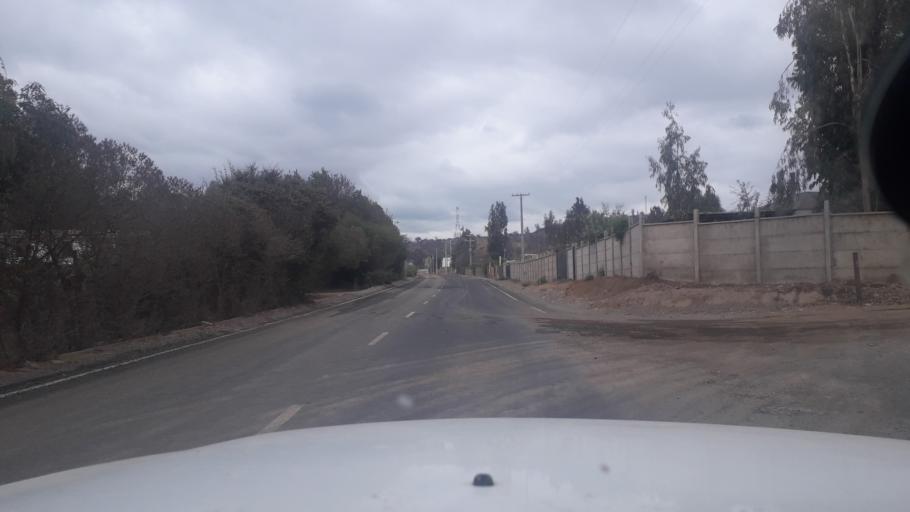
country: CL
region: Valparaiso
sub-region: Provincia de Marga Marga
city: Limache
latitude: -33.0283
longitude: -71.2755
